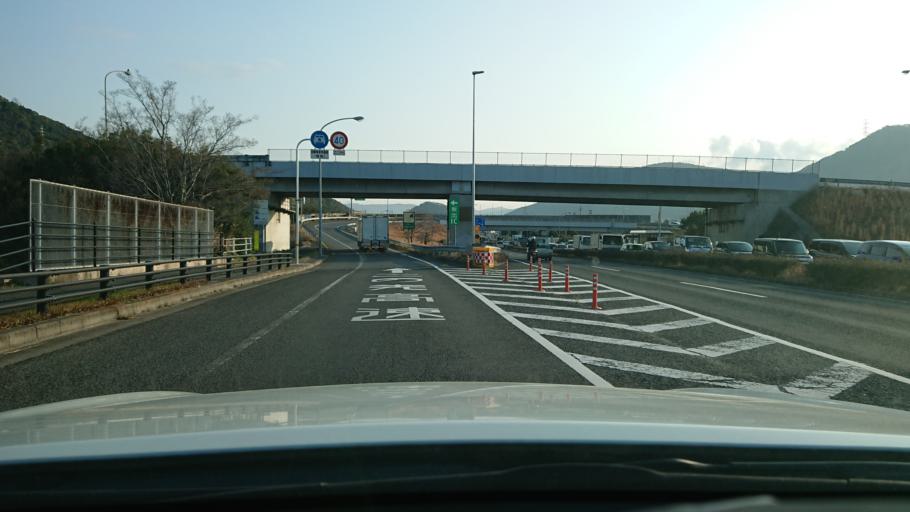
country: JP
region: Kagawa
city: Sakaidecho
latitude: 34.2976
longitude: 133.8405
